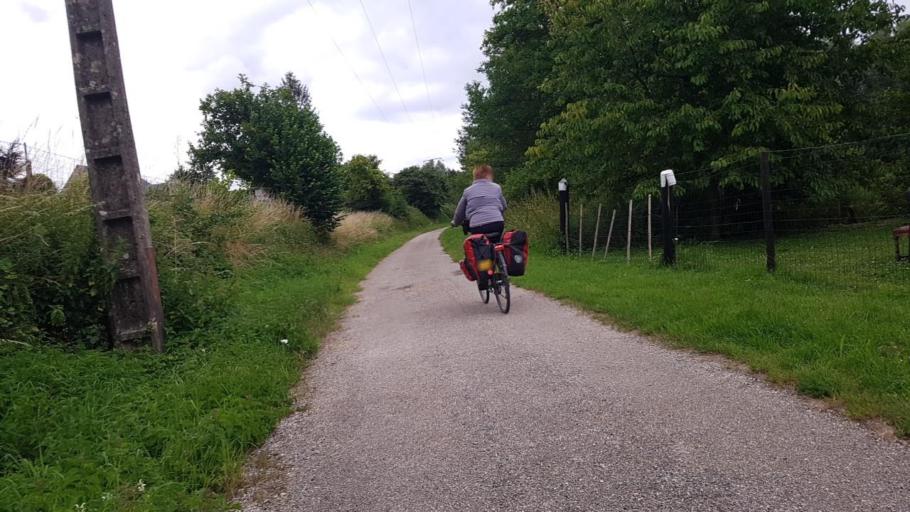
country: FR
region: Picardie
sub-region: Departement de l'Aisne
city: Origny-en-Thierache
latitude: 49.9247
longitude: 3.9641
